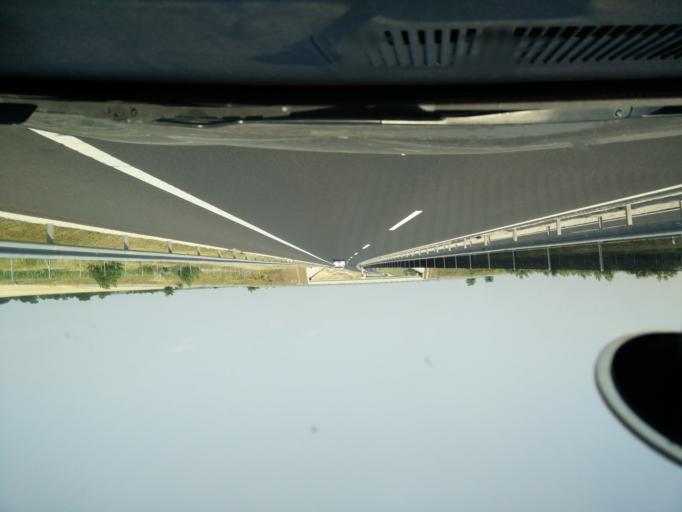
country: HU
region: Tolna
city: Tengelic
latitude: 46.4840
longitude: 18.7453
